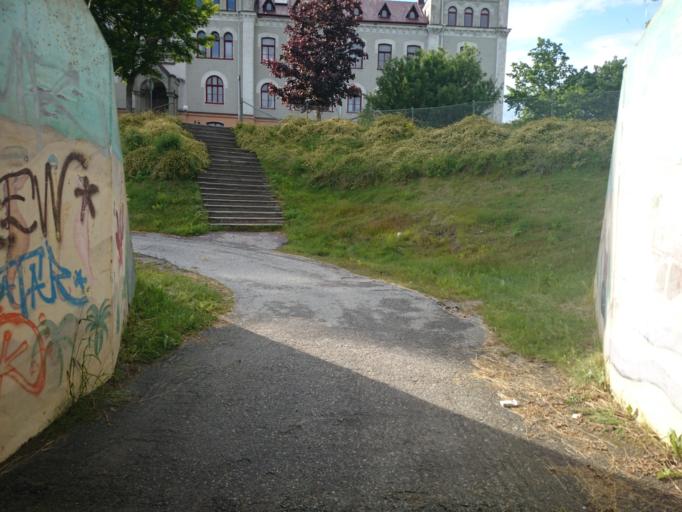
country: SE
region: Vaesternorrland
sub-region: Haernoesands Kommun
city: Haernoesand
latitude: 62.6241
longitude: 17.9240
